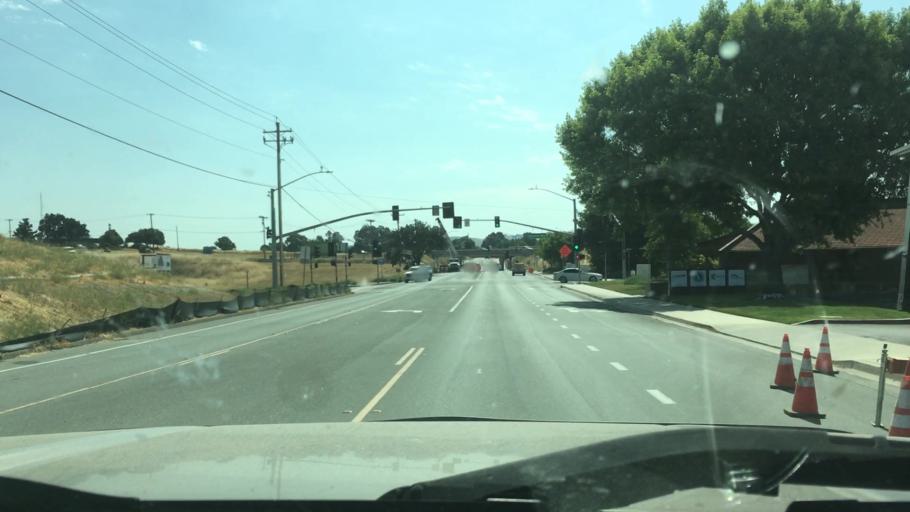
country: US
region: California
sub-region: San Luis Obispo County
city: Templeton
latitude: 35.5544
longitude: -120.7152
